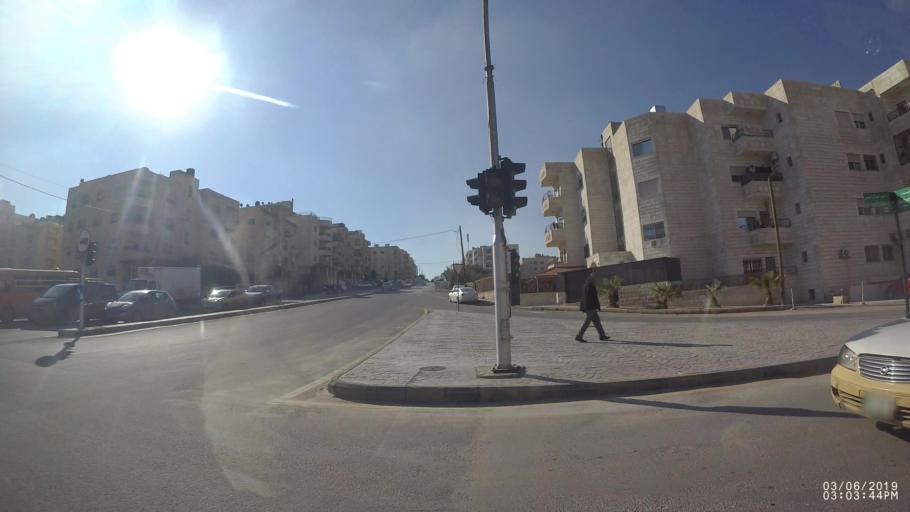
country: JO
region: Amman
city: Amman
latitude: 31.9863
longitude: 35.9428
